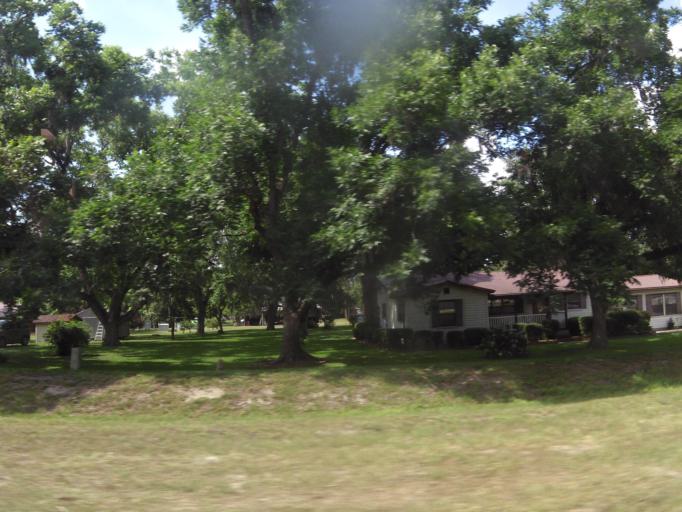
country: US
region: Florida
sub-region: Baker County
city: Macclenny
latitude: 30.2012
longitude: -82.0428
